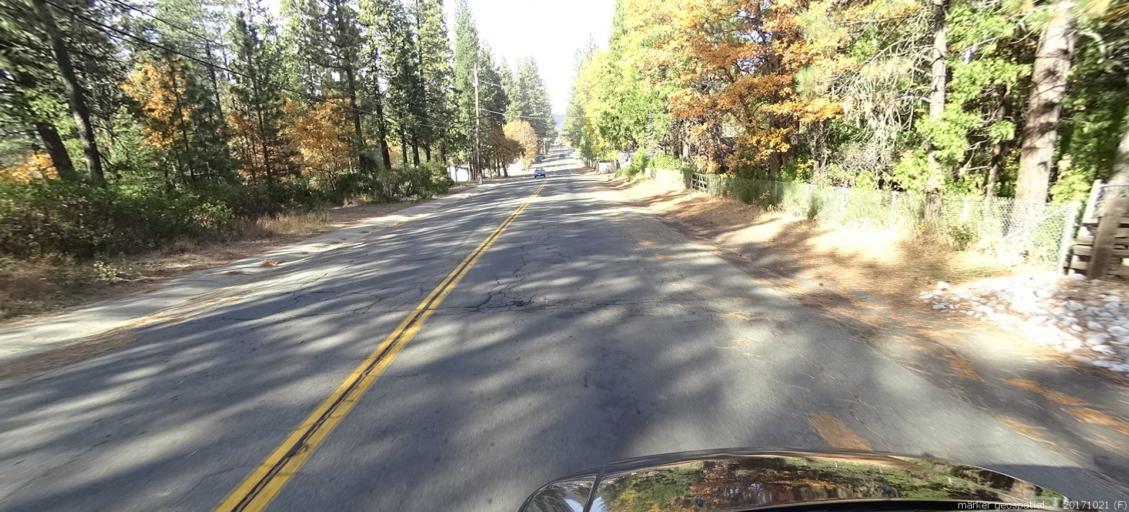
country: US
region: California
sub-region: Shasta County
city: Burney
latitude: 40.8760
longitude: -121.6613
